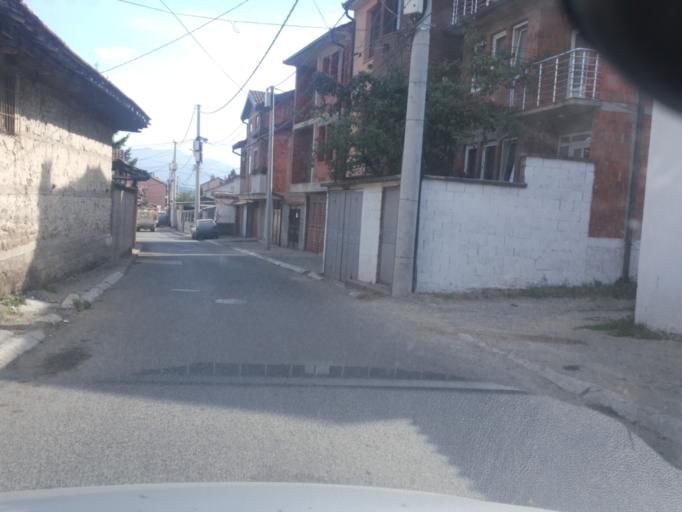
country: XK
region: Gjakova
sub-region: Komuna e Gjakoves
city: Gjakove
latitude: 42.3792
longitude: 20.4246
